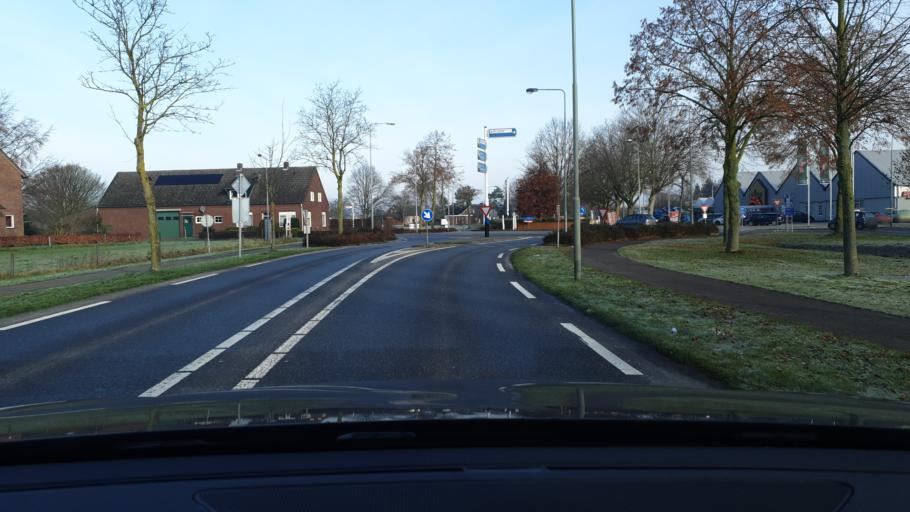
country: NL
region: Limburg
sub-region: Gemeente Peel en Maas
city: Maasbree
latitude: 51.4246
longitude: 6.0353
